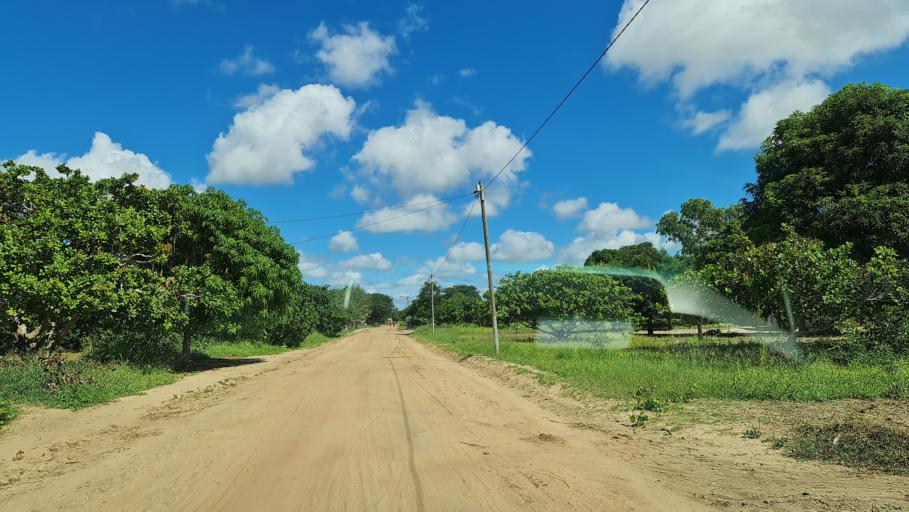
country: MZ
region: Nampula
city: Ilha de Mocambique
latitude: -15.5575
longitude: 40.4130
